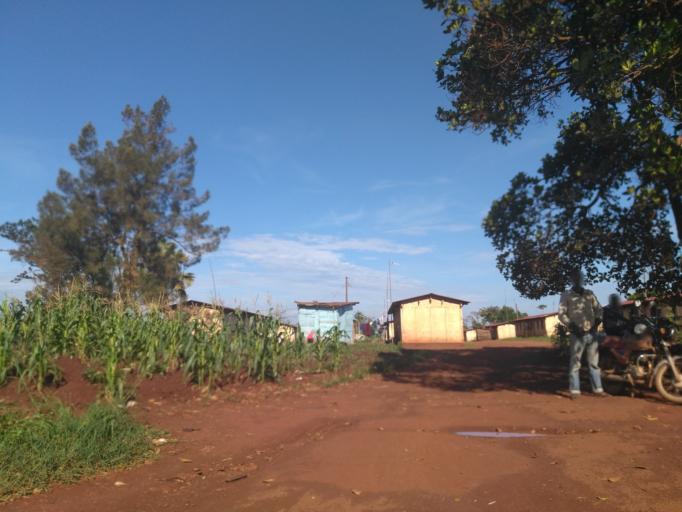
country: UG
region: Eastern Region
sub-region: Jinja District
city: Jinja
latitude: 0.4420
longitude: 33.2132
